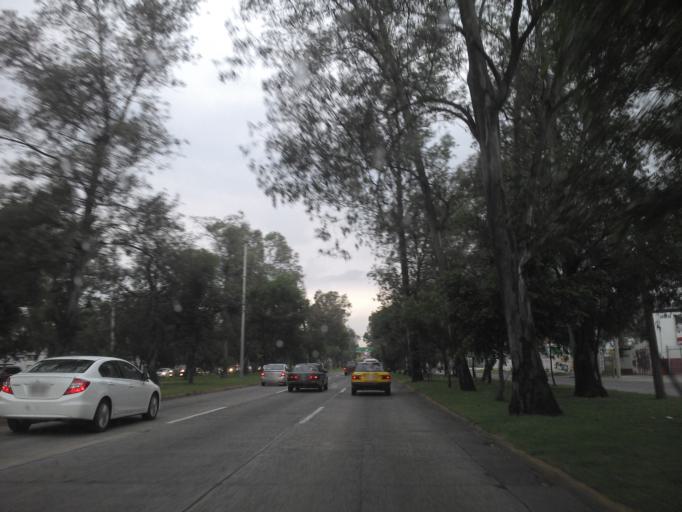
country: MX
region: Jalisco
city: Tlaquepaque
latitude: 20.6338
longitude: -103.3393
